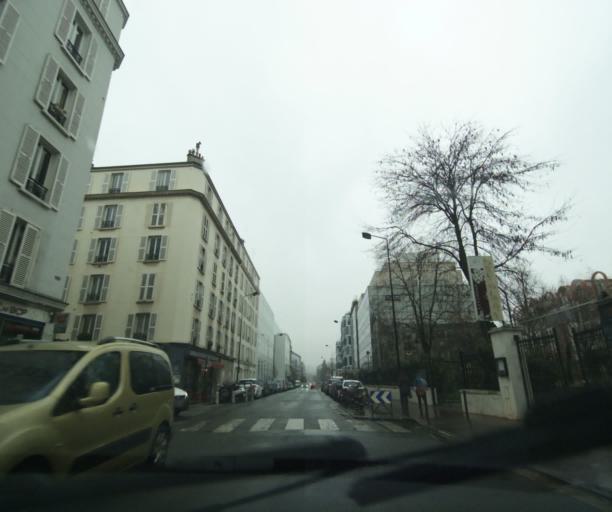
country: FR
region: Ile-de-France
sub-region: Departement des Hauts-de-Seine
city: Levallois-Perret
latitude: 48.8905
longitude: 2.2793
